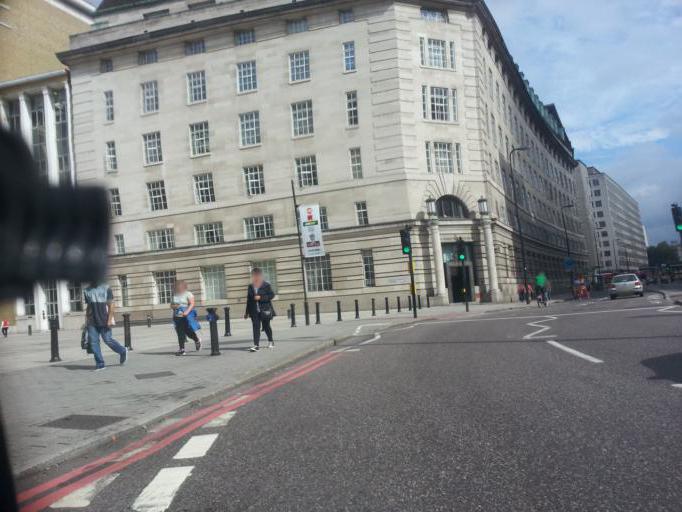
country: GB
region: England
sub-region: Greater London
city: City of Westminster
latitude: 51.5009
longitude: -0.1159
